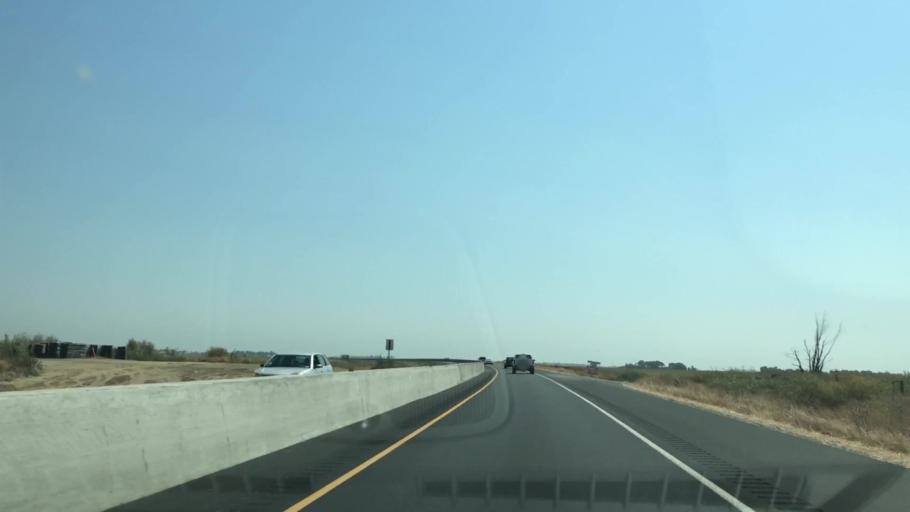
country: US
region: California
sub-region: Contra Costa County
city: Bethel Island
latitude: 38.1147
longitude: -121.5546
